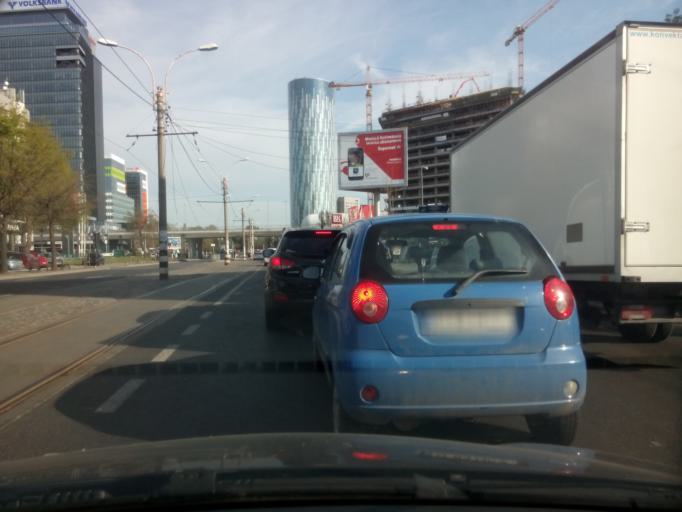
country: RO
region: Bucuresti
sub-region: Municipiul Bucuresti
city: Bucharest
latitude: 44.4813
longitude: 26.1012
